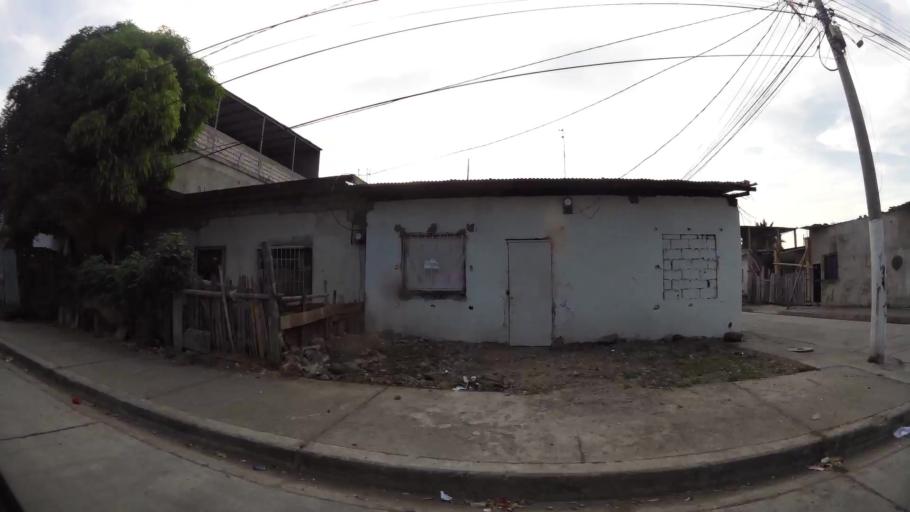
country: EC
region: Guayas
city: Eloy Alfaro
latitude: -2.0925
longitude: -79.9095
